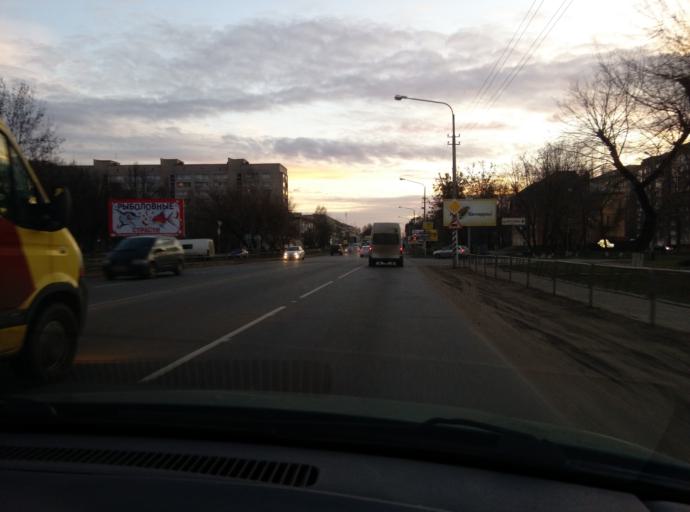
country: BY
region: Minsk
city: Horad Barysaw
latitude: 54.2185
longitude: 28.4908
